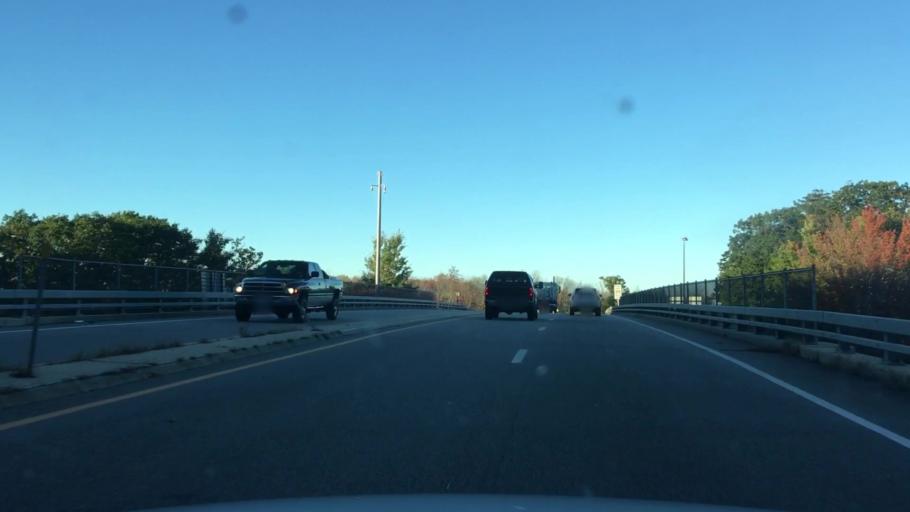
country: US
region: New Hampshire
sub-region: Rockingham County
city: Hampton
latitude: 42.9613
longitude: -70.8637
